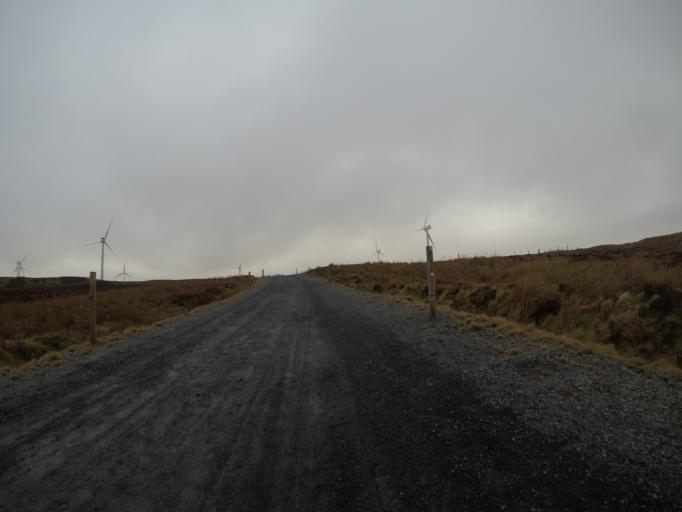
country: GB
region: Scotland
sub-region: North Ayrshire
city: Fairlie
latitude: 55.7545
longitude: -4.7949
